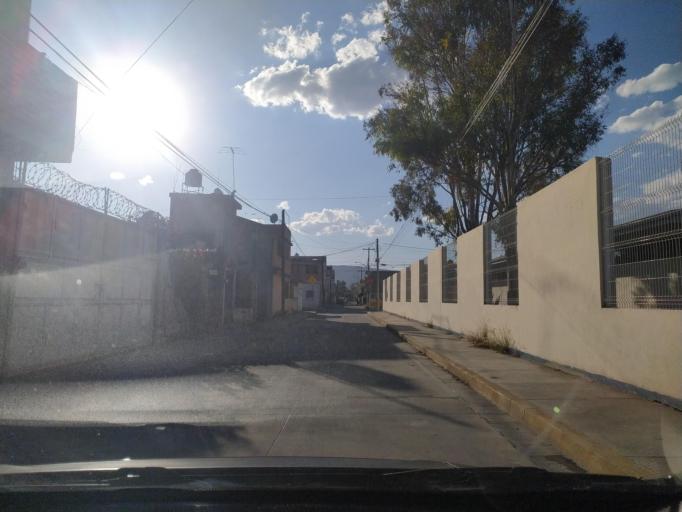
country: MX
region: Guanajuato
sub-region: San Francisco del Rincon
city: Fraccionamiento la Mezquitera
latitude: 21.0108
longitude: -101.8403
